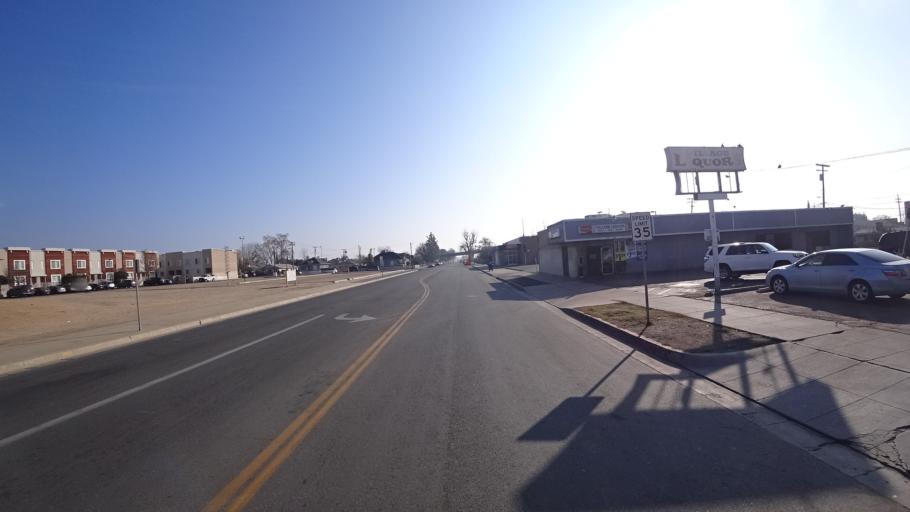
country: US
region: California
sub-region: Kern County
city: Bakersfield
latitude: 35.3787
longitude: -118.9918
